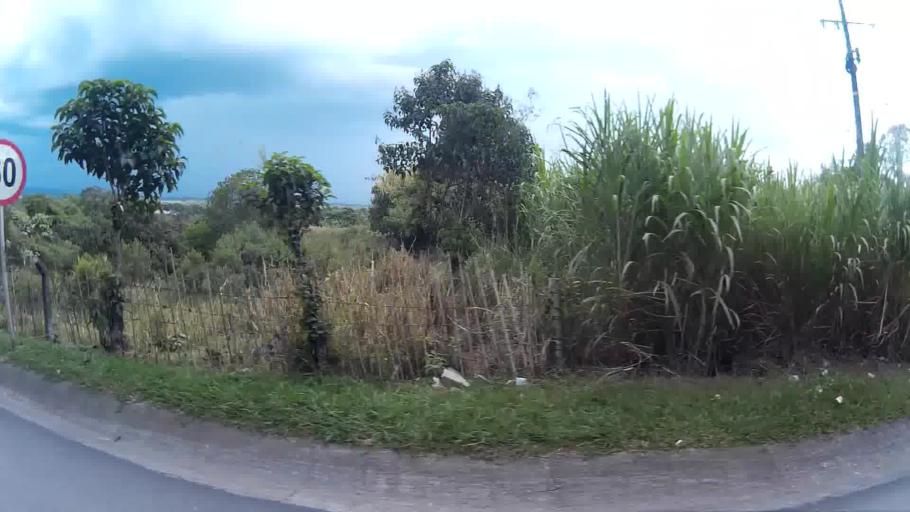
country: CO
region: Risaralda
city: Pereira
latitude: 4.8124
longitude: -75.7777
